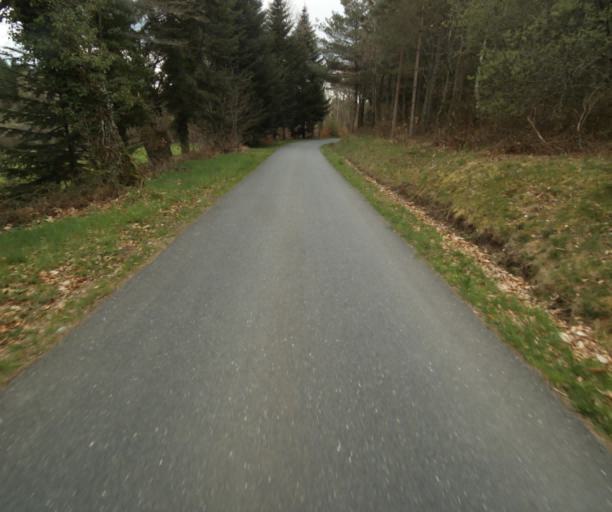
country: FR
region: Limousin
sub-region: Departement de la Correze
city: Correze
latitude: 45.3071
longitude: 1.9048
